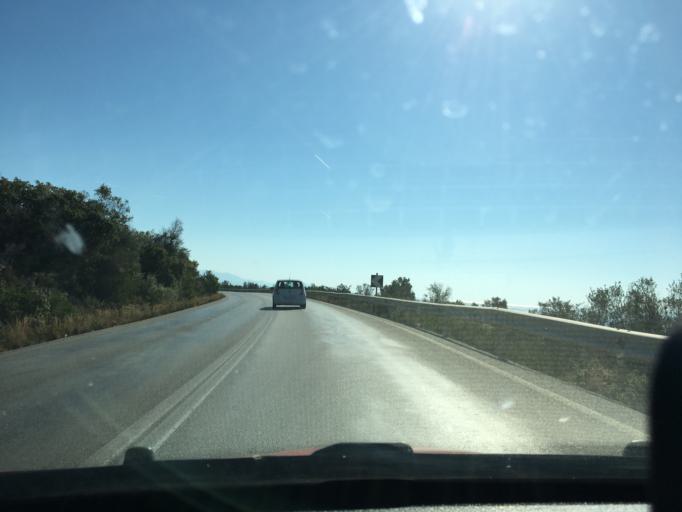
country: GR
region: Central Macedonia
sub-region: Nomos Chalkidikis
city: Ormylia
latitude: 40.2612
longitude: 23.4739
